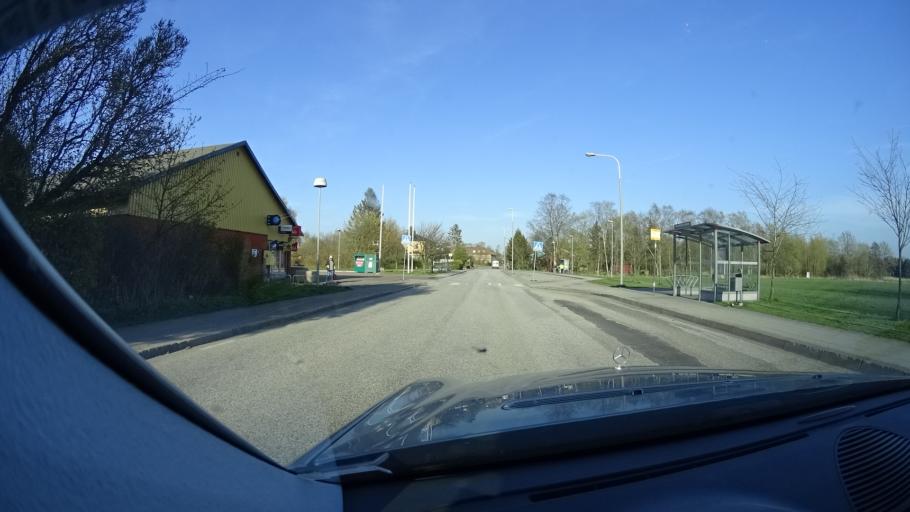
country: SE
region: Skane
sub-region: Svalovs Kommun
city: Svaloev
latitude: 55.8633
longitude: 13.1533
